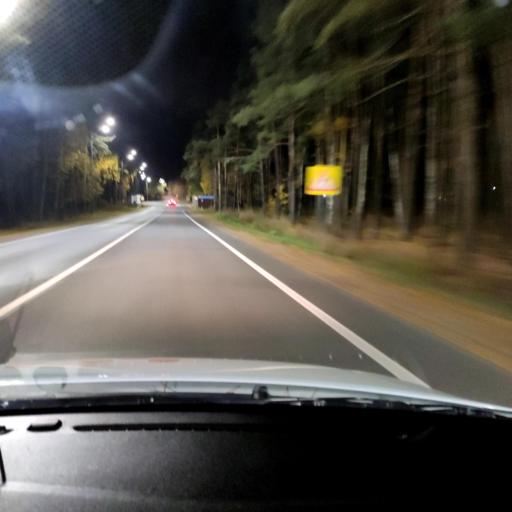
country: RU
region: Tatarstan
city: Verkhniy Uslon
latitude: 55.6397
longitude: 49.0273
